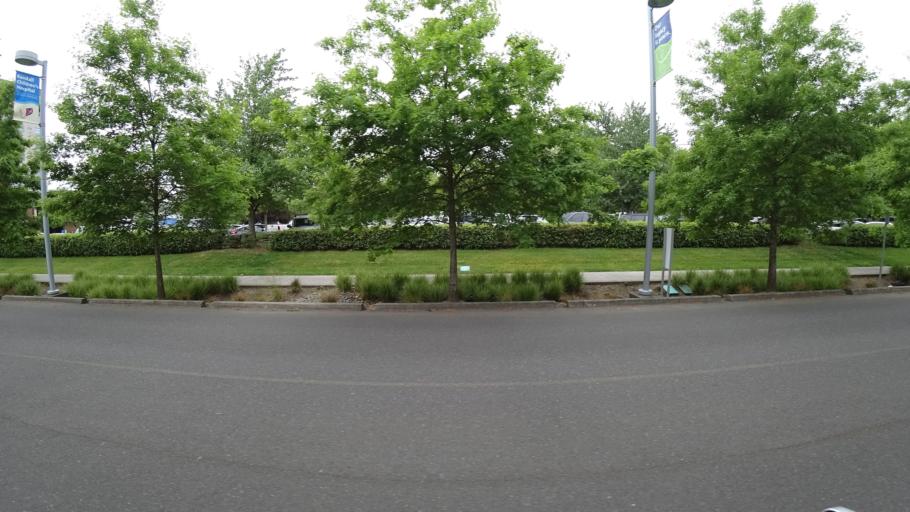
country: US
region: Oregon
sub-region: Multnomah County
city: Portland
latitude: 45.5459
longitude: -122.6695
